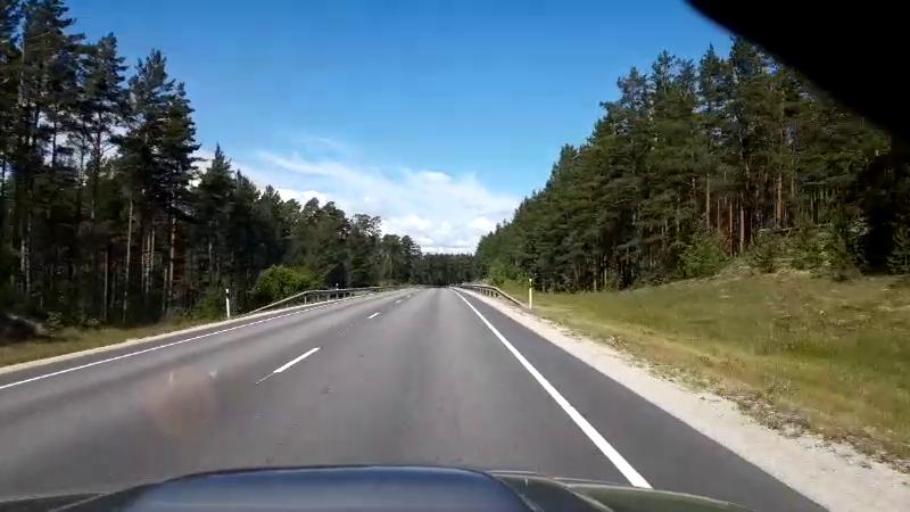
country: EE
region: Paernumaa
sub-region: Paernu linn
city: Parnu
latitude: 58.1388
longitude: 24.5077
